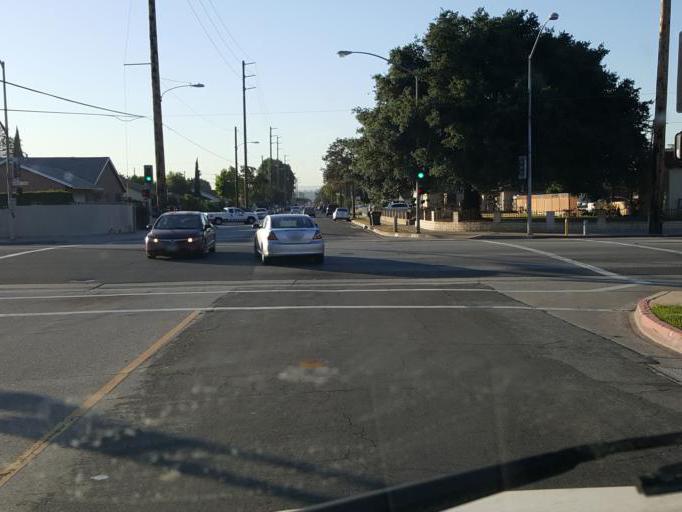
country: US
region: California
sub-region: Los Angeles County
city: West Puente Valley
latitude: 34.0494
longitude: -117.9594
